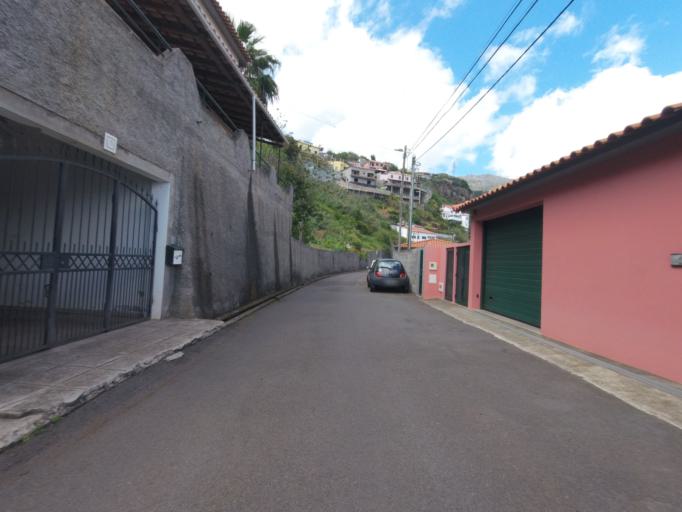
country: PT
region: Madeira
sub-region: Funchal
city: Nossa Senhora do Monte
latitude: 32.6693
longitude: -16.9208
